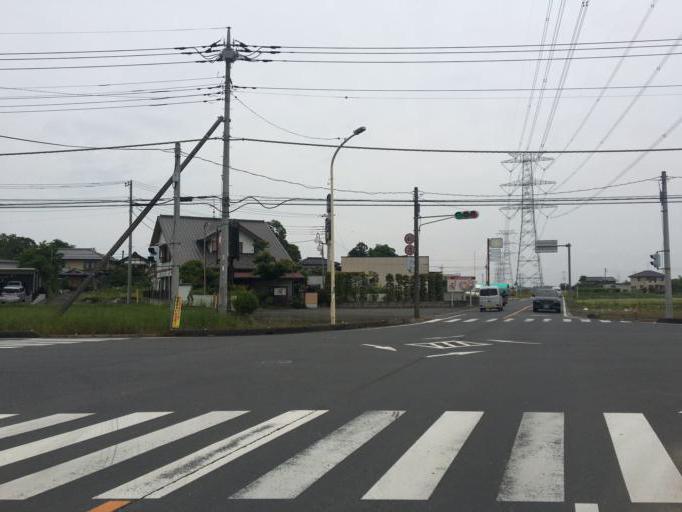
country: JP
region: Saitama
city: Konosu
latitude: 36.0255
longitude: 139.4578
